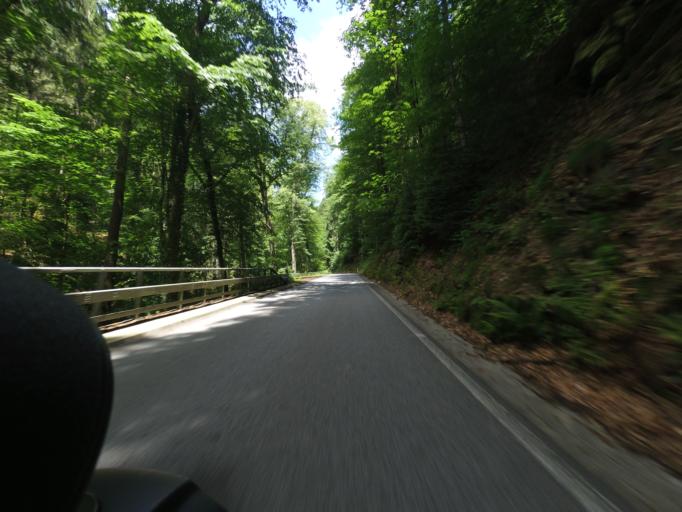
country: DE
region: Saxony
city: Porschdorf
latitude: 50.9499
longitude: 14.1356
